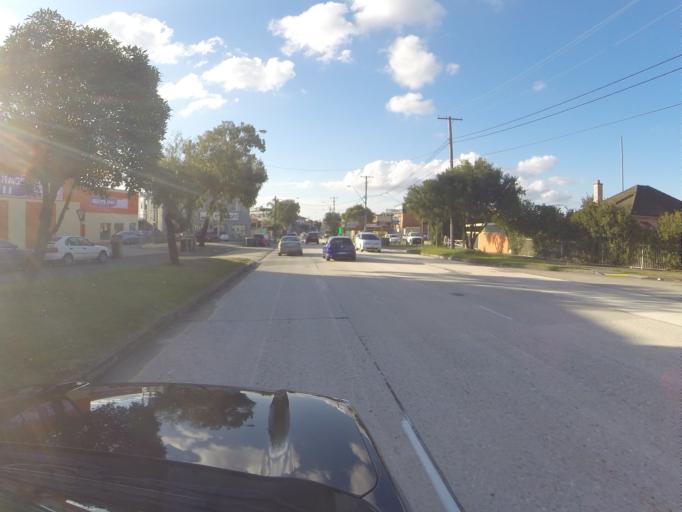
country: AU
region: New South Wales
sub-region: Rockdale
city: Bexley
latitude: -33.9588
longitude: 151.1176
